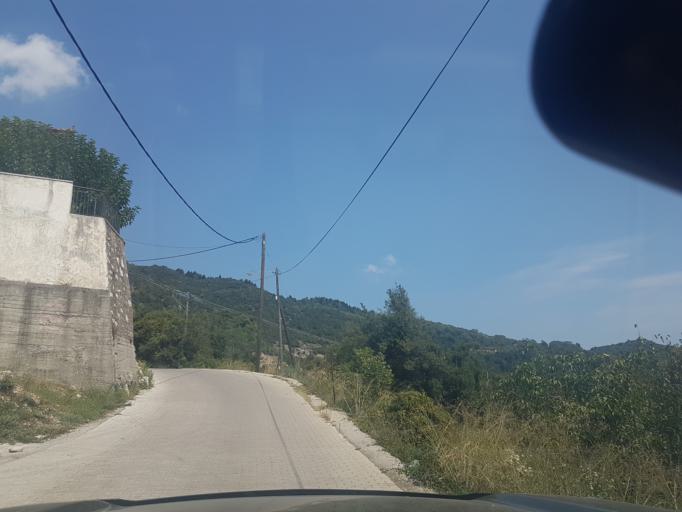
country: GR
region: Central Greece
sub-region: Nomos Evvoias
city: Yimnon
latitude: 38.6189
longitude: 23.8882
